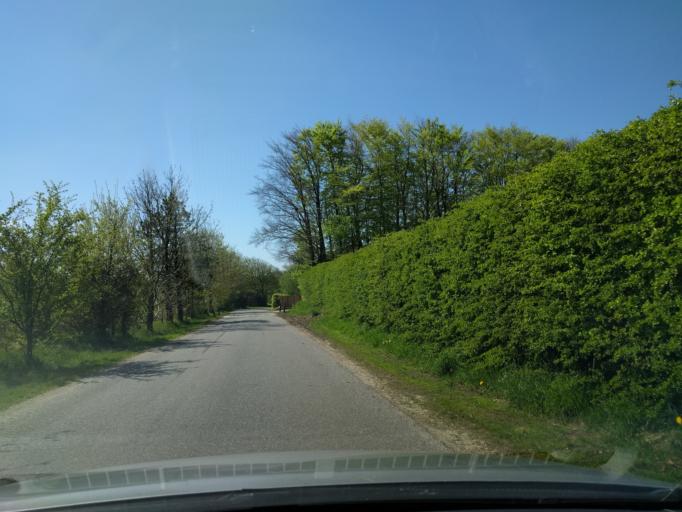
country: DK
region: South Denmark
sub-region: Varde Kommune
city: Olgod
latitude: 55.7840
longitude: 8.6568
